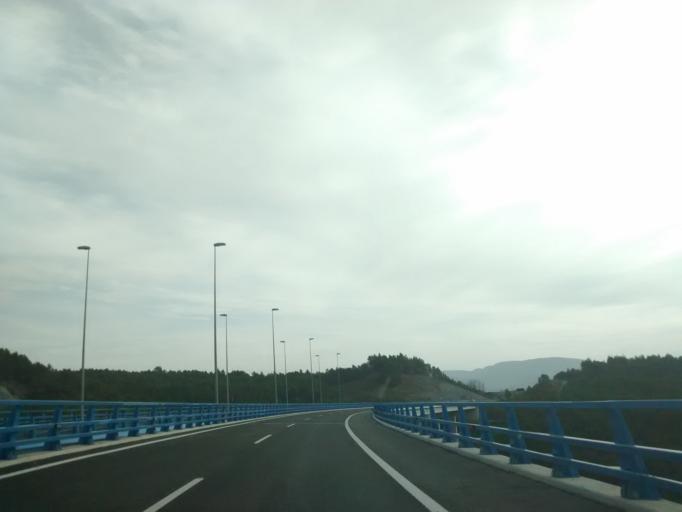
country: ES
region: Navarre
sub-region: Provincia de Navarra
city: Yesa
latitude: 42.6256
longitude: -1.1732
